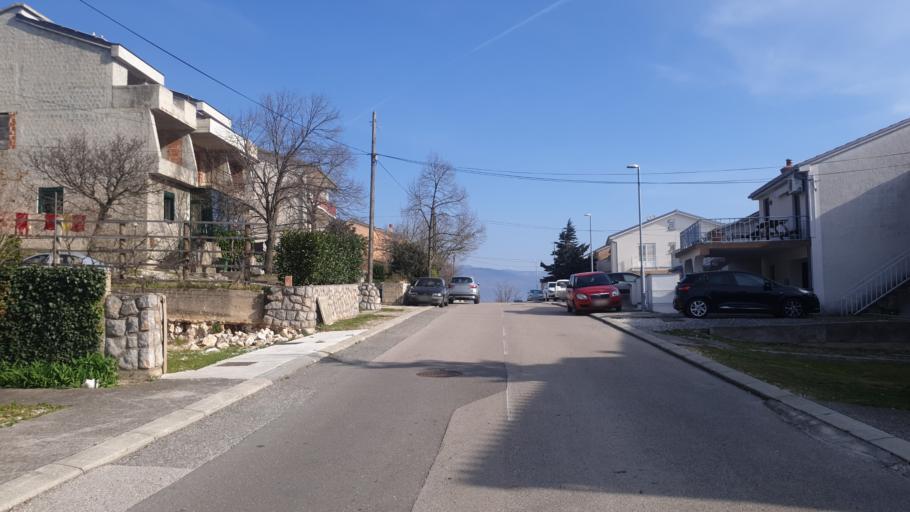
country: HR
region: Primorsko-Goranska
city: Novi Vinodolski
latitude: 45.1287
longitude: 14.7961
